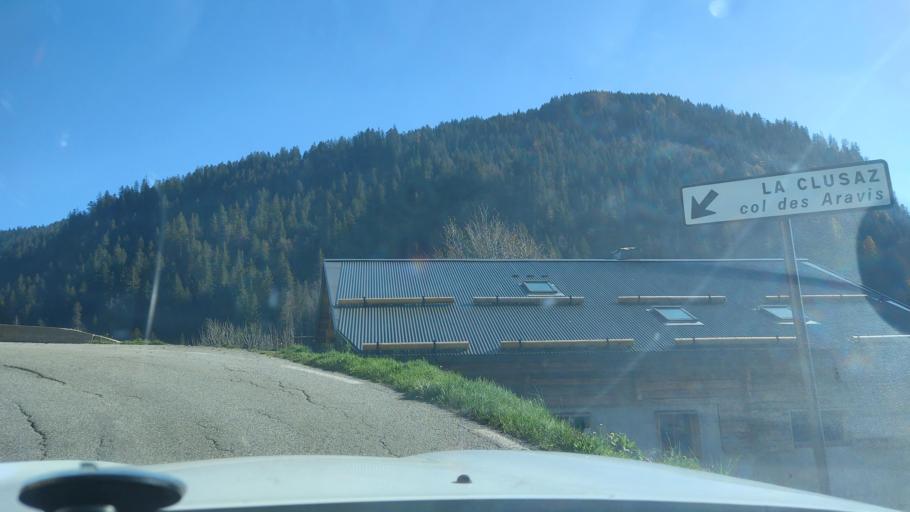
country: FR
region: Rhone-Alpes
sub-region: Departement de la Haute-Savoie
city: La Clusaz
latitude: 45.8641
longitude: 6.4951
